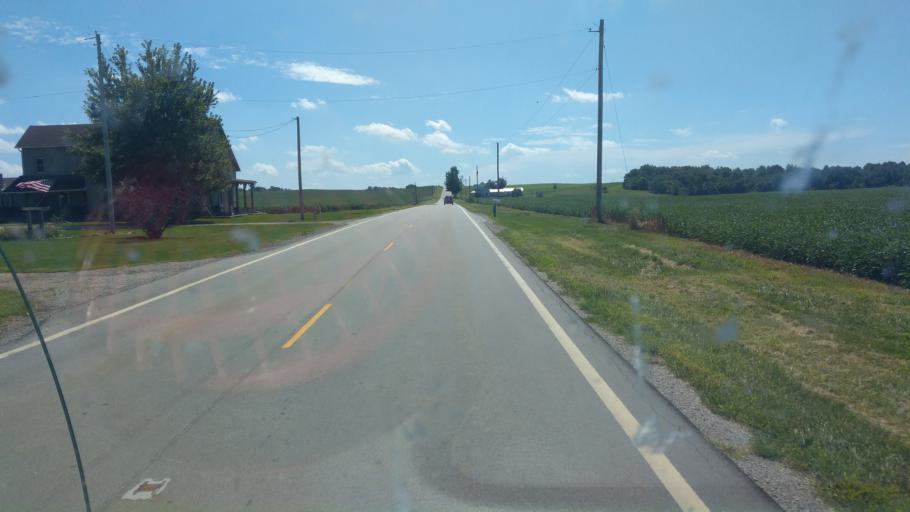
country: US
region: Ohio
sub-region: Marion County
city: Marion
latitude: 40.7456
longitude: -83.1308
